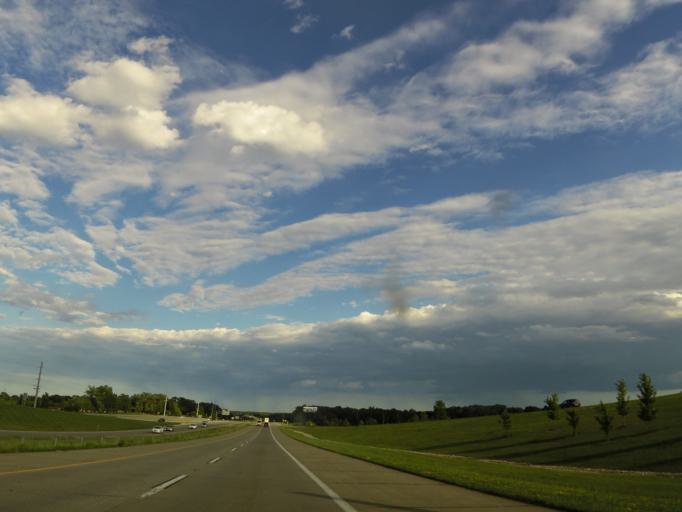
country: US
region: Missouri
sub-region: Saint Charles County
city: Dardenne Prairie
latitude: 38.7485
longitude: -90.7532
